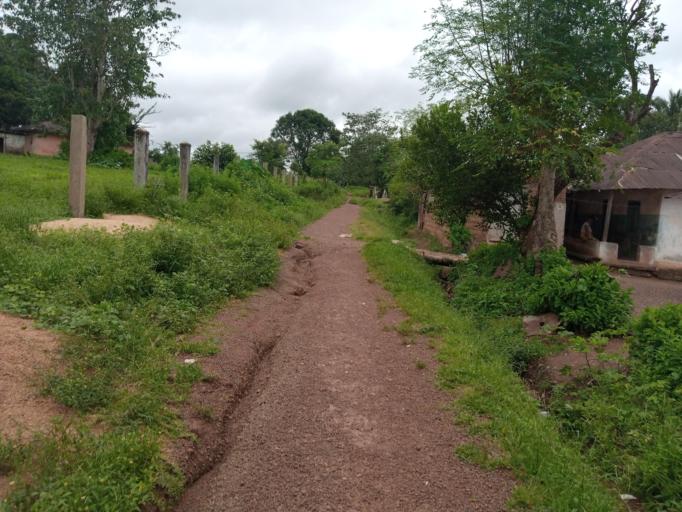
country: SL
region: Southern Province
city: Largo
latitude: 8.2033
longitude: -12.0609
